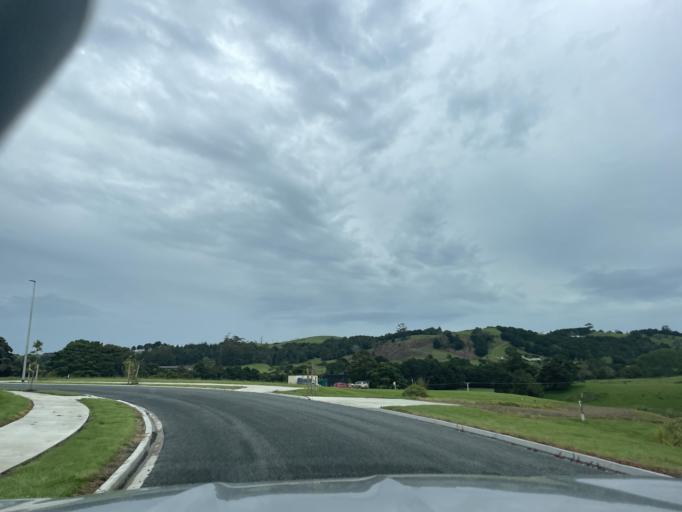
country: NZ
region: Northland
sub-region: Whangarei
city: Ruakaka
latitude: -36.0979
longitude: 174.2308
